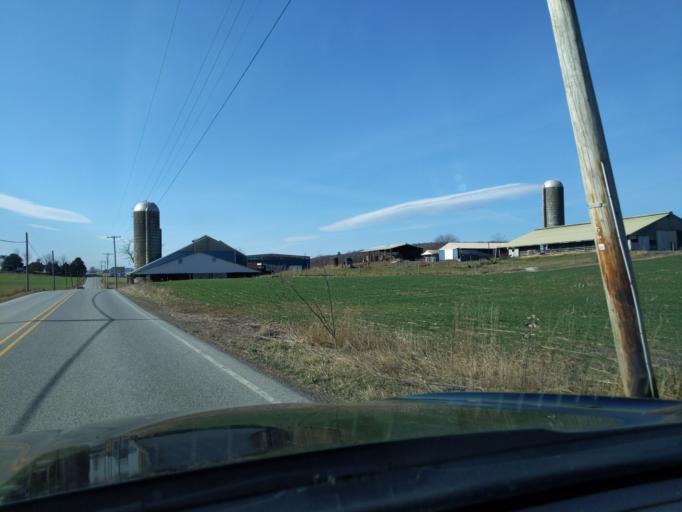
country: US
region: Pennsylvania
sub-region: Blair County
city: Martinsburg
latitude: 40.3467
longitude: -78.2576
